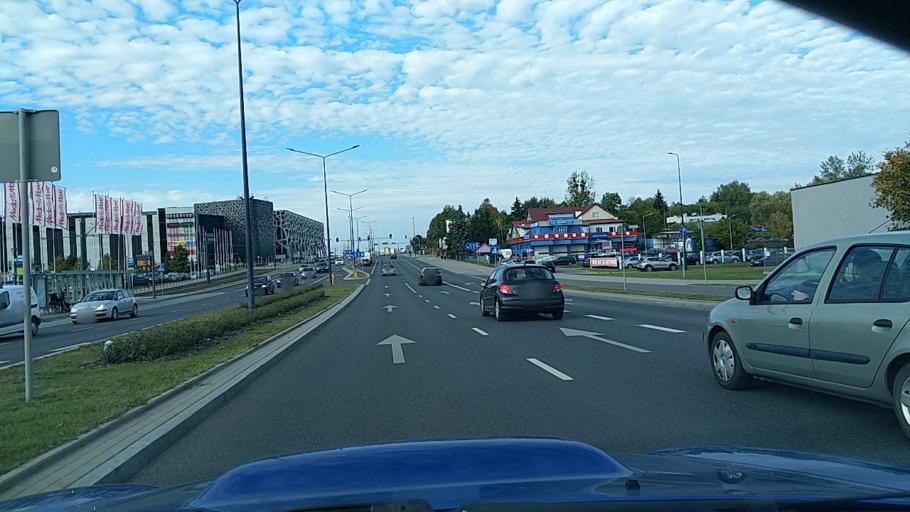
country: PL
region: Warmian-Masurian Voivodeship
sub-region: Powiat olsztynski
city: Olsztyn
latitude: 53.7508
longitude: 20.4864
